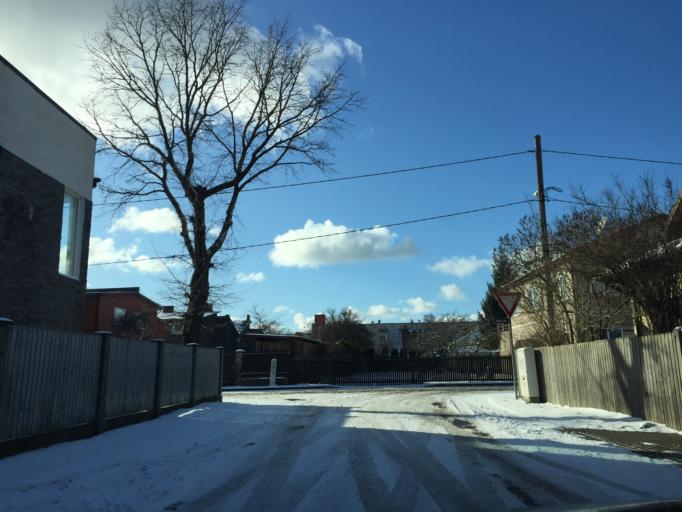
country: LV
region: Ventspils
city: Ventspils
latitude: 57.3845
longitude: 21.5542
